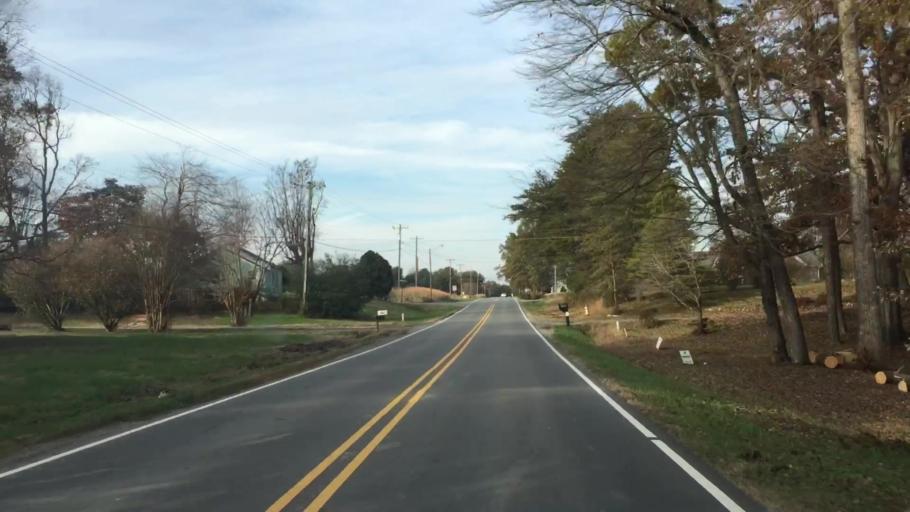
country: US
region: North Carolina
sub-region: Rockingham County
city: Reidsville
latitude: 36.3424
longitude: -79.6996
